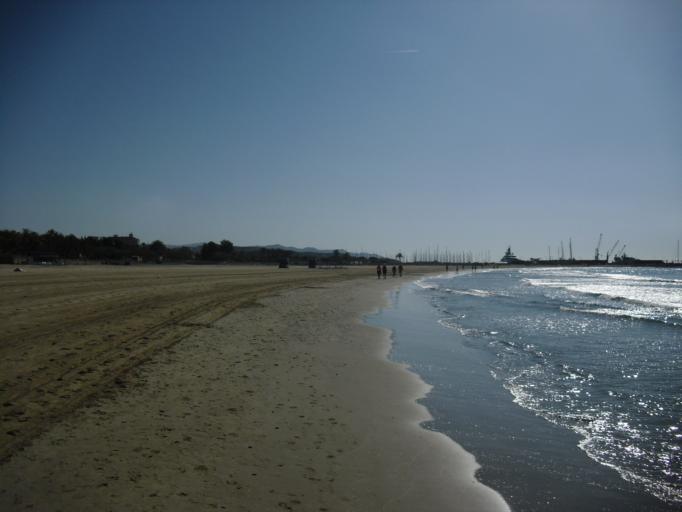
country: ES
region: Catalonia
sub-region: Provincia de Barcelona
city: Vilanova i la Geltru
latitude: 41.2116
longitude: 1.7209
